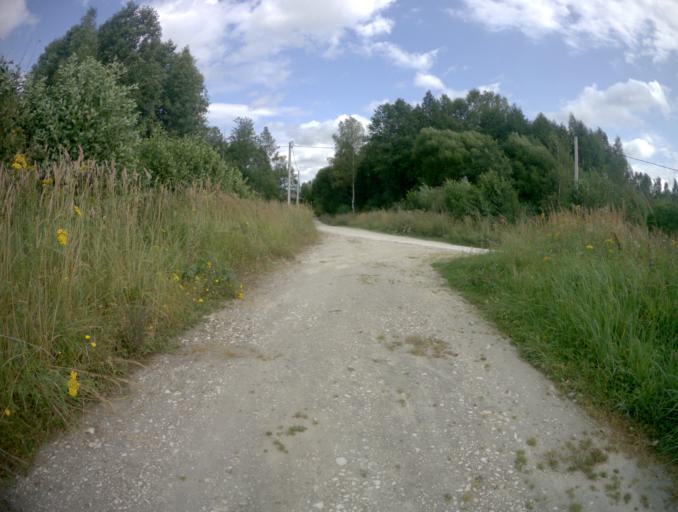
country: RU
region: Vladimir
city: Golovino
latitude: 55.9051
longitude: 40.5304
